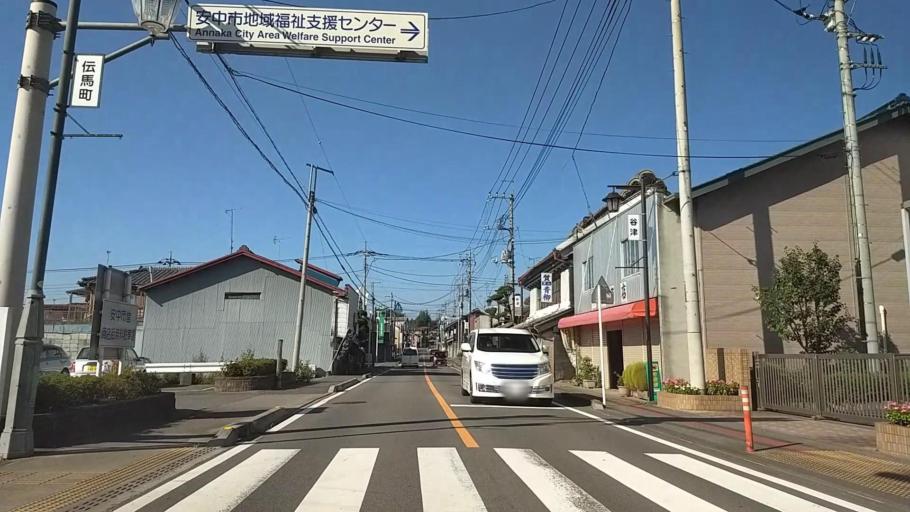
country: JP
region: Gunma
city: Annaka
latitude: 36.3283
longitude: 138.8979
